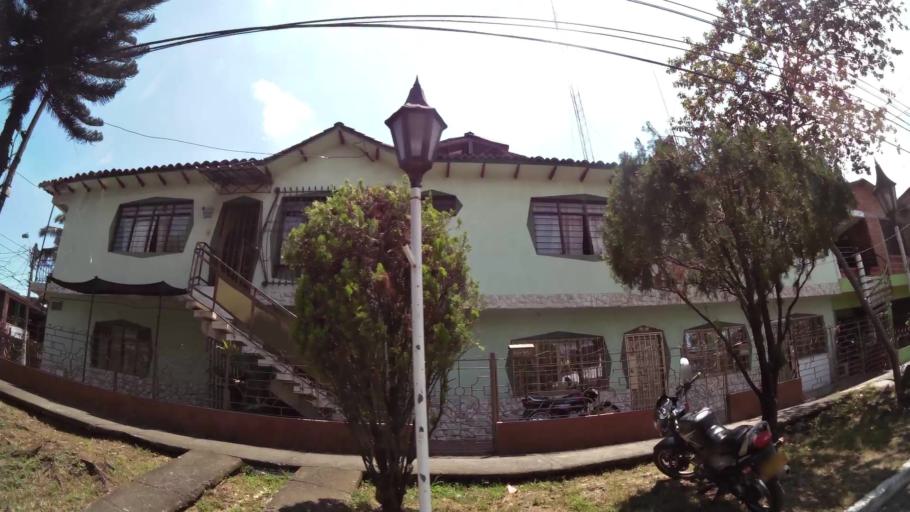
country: CO
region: Valle del Cauca
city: Cali
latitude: 3.4473
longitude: -76.4971
